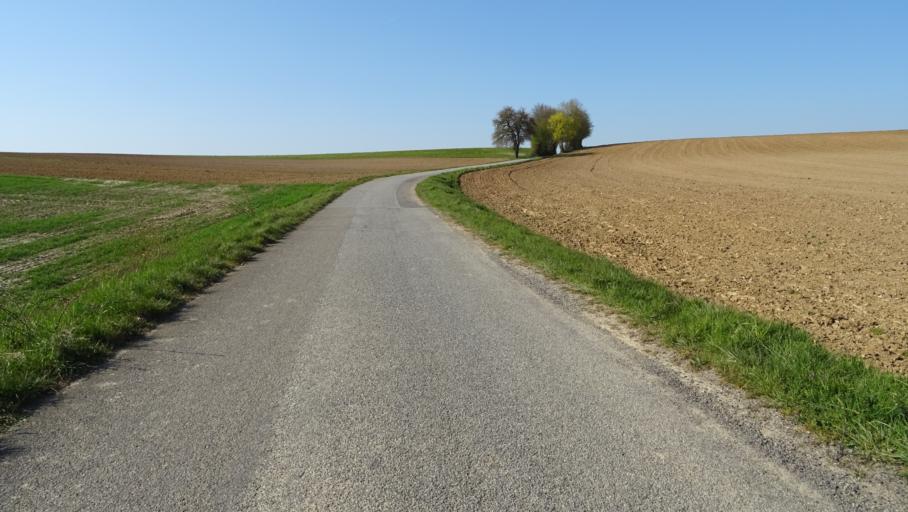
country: DE
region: Baden-Wuerttemberg
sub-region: Karlsruhe Region
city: Billigheim
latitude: 49.3779
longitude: 9.2300
